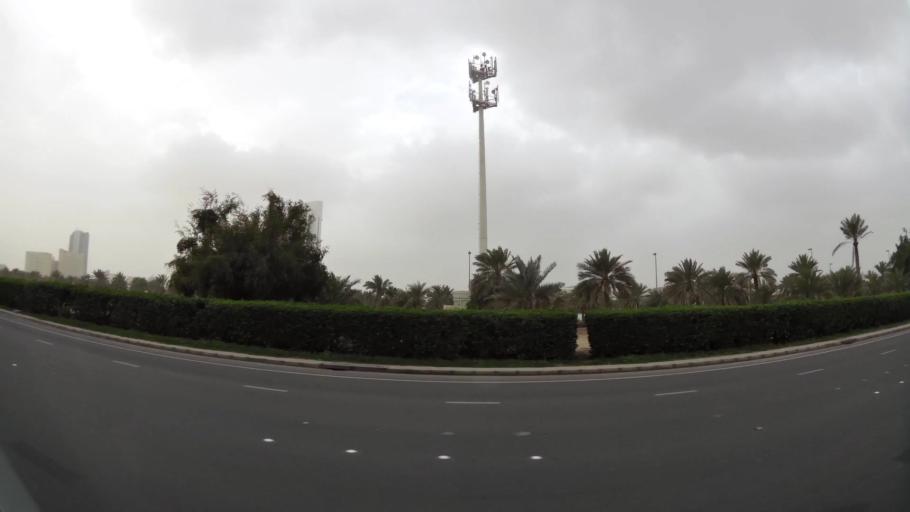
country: AE
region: Abu Dhabi
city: Abu Dhabi
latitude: 24.4655
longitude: 54.3964
